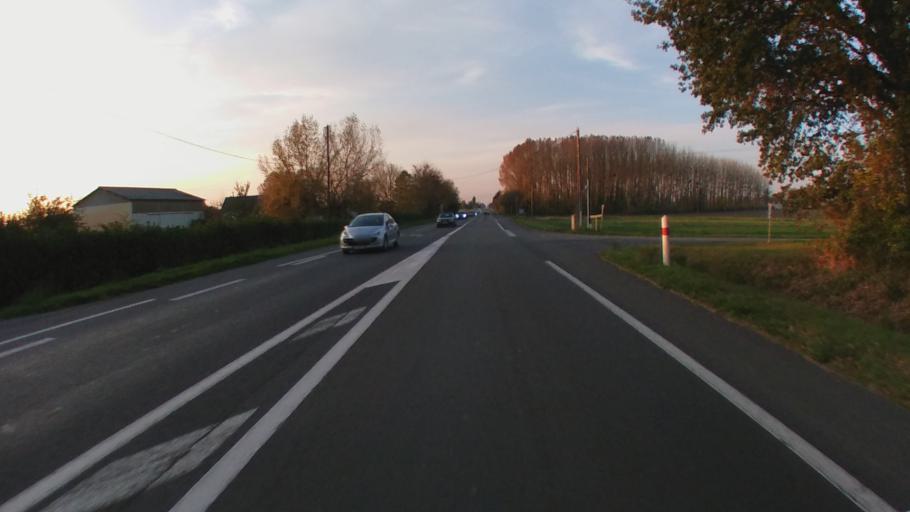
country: FR
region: Pays de la Loire
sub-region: Departement de Maine-et-Loire
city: Vivy
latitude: 47.3395
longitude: -0.0689
